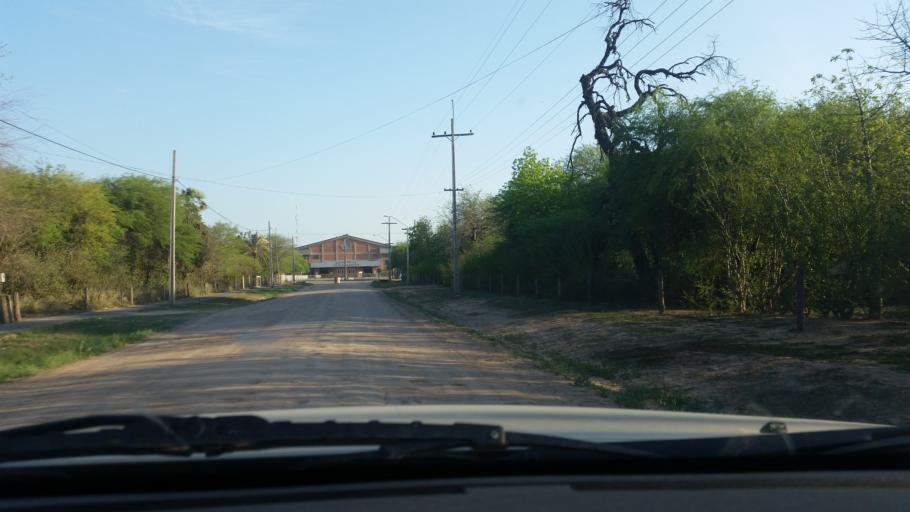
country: PY
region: Boqueron
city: Filadelfia
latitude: -22.3511
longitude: -60.0388
